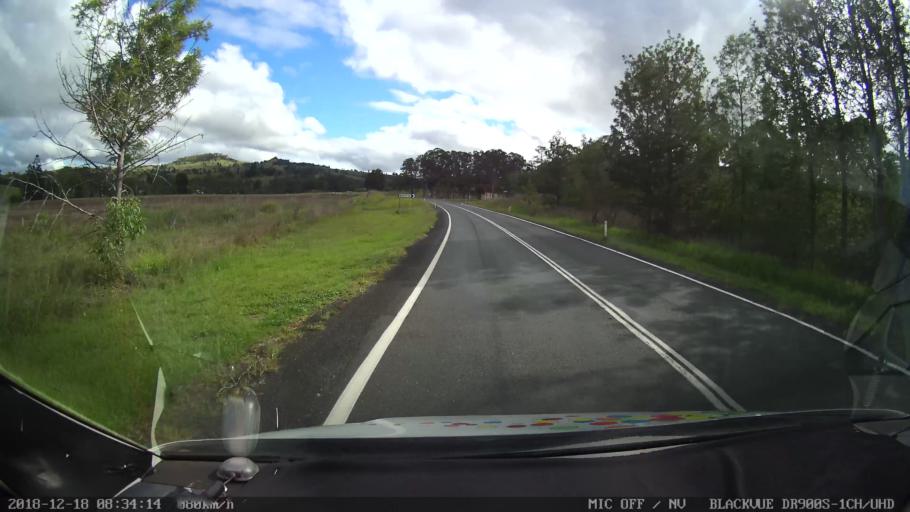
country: AU
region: New South Wales
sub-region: Kyogle
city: Kyogle
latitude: -28.2854
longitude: 152.7912
